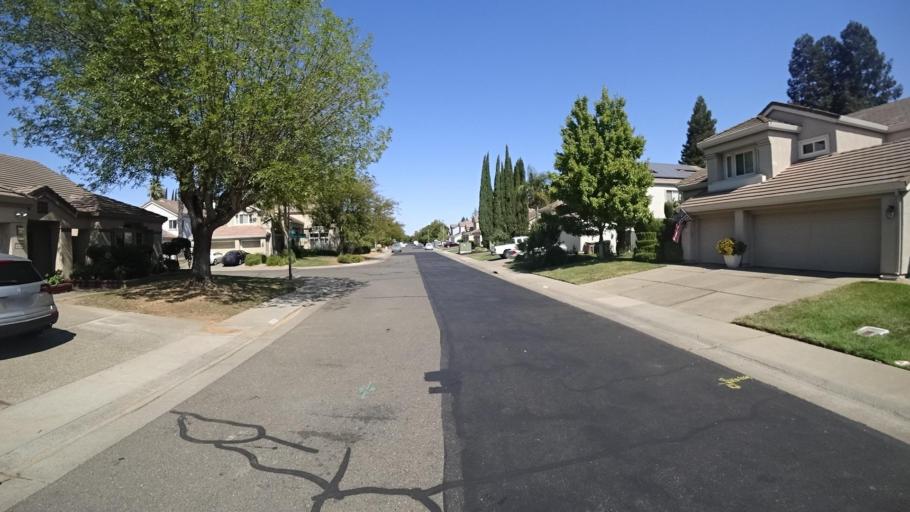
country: US
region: California
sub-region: Sacramento County
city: Laguna
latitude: 38.4132
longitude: -121.4092
